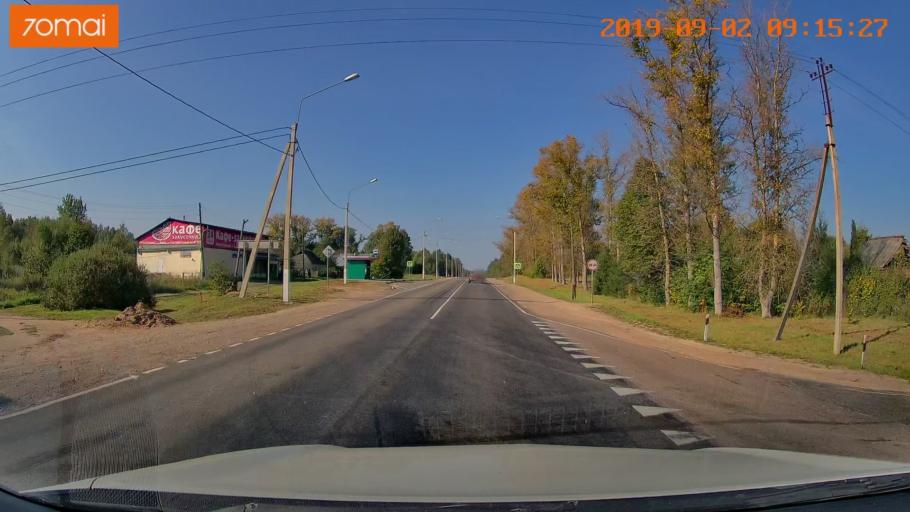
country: RU
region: Kaluga
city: Nikola-Lenivets
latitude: 54.8388
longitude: 35.4933
